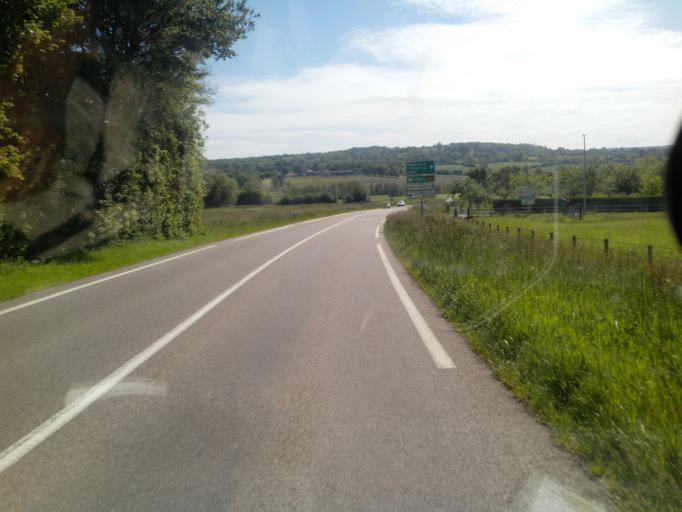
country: FR
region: Lower Normandy
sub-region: Departement du Calvados
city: Saint-Gatien-des-Bois
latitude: 49.3068
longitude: 0.2584
